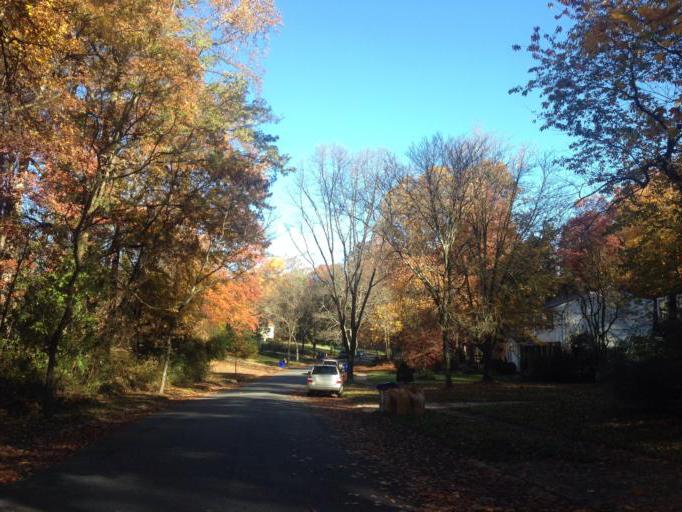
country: US
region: Maryland
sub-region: Howard County
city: Riverside
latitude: 39.1917
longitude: -76.8789
